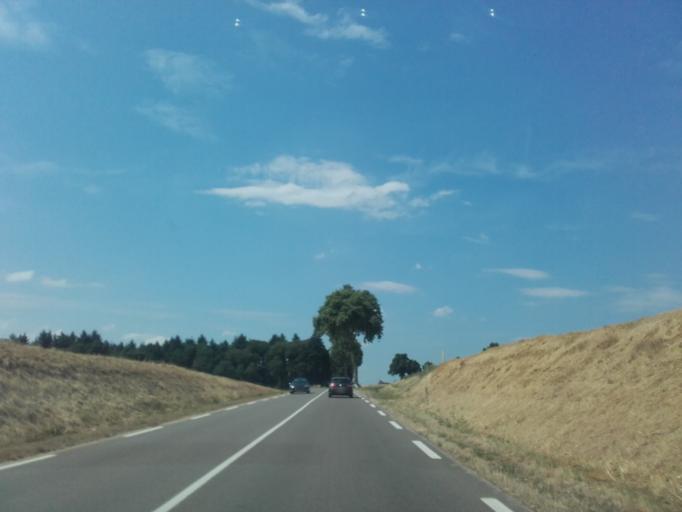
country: FR
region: Rhone-Alpes
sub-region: Departement de l'Ain
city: Meximieux
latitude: 45.9266
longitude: 5.1866
